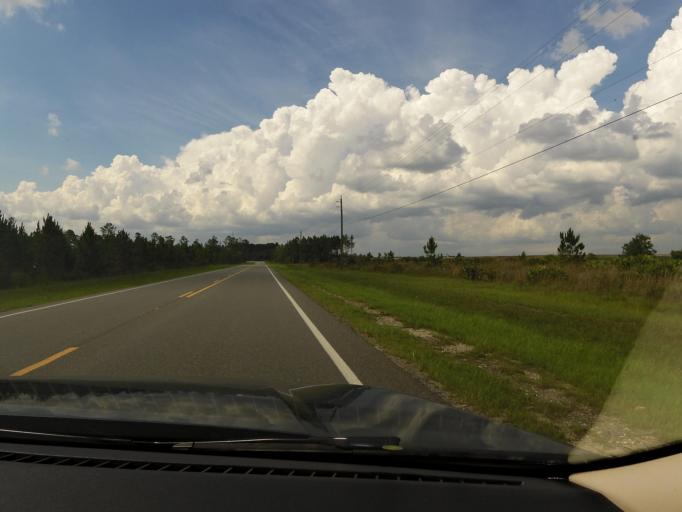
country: US
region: Florida
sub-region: Baker County
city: Macclenny
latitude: 30.2389
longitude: -82.0774
